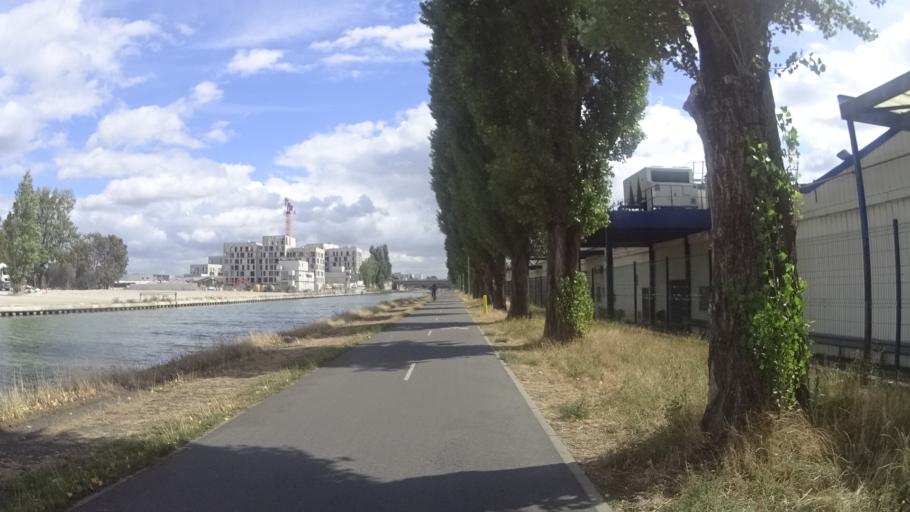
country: FR
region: Ile-de-France
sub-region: Departement de Seine-Saint-Denis
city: Bondy
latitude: 48.9063
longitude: 2.4765
